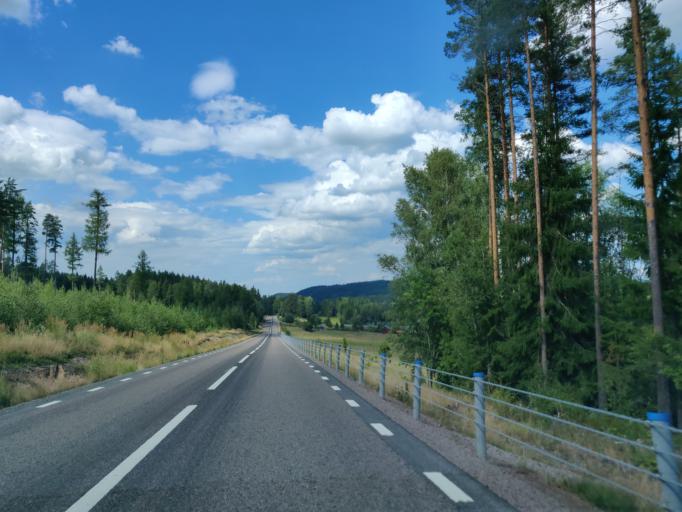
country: SE
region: Vaermland
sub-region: Hagfors Kommun
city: Hagfors
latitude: 59.8752
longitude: 13.7076
